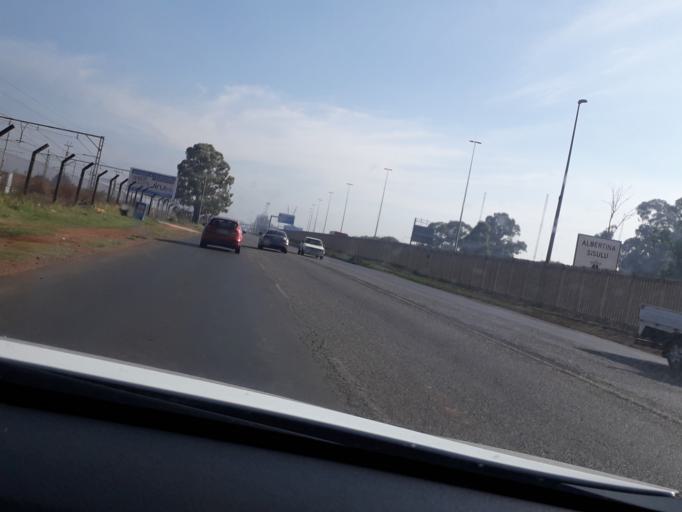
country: ZA
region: Gauteng
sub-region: City of Johannesburg Metropolitan Municipality
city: Modderfontein
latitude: -26.1432
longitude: 28.2194
